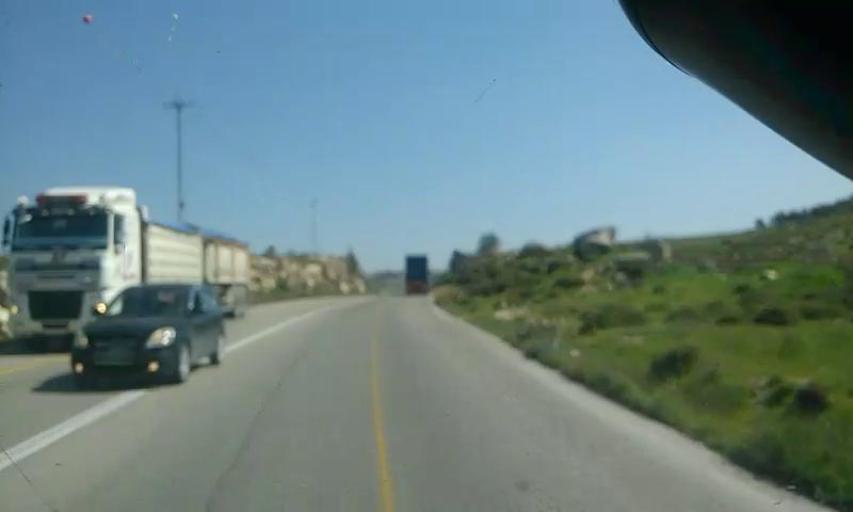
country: PS
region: West Bank
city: Tarqumya
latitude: 31.5611
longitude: 35.0037
